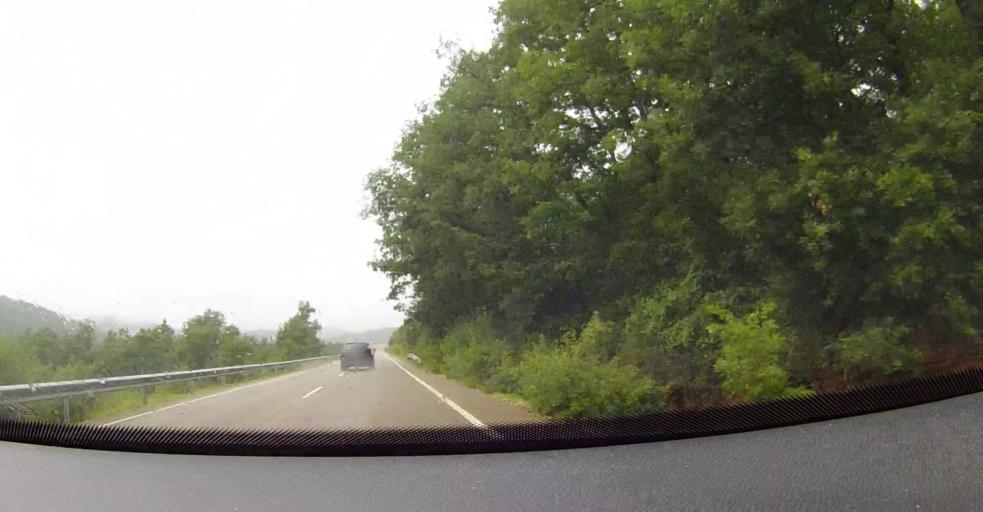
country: ES
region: Castille and Leon
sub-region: Provincia de Leon
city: Sabero
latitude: 42.8389
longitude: -5.2338
